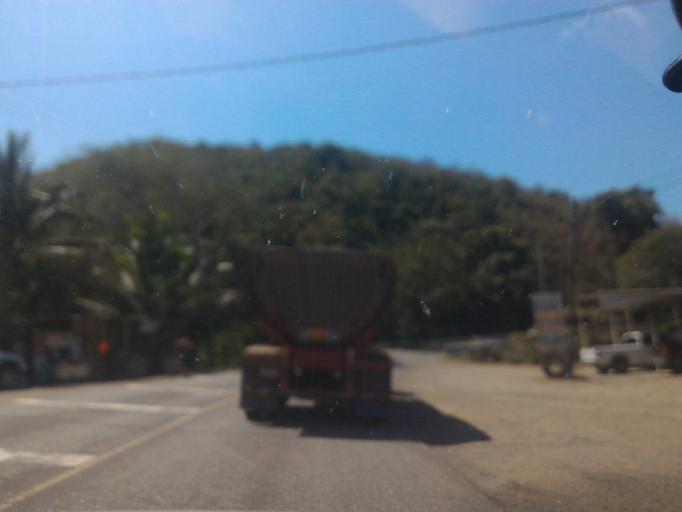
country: MX
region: Michoacan
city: Coahuayana Viejo
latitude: 18.6274
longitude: -103.6697
